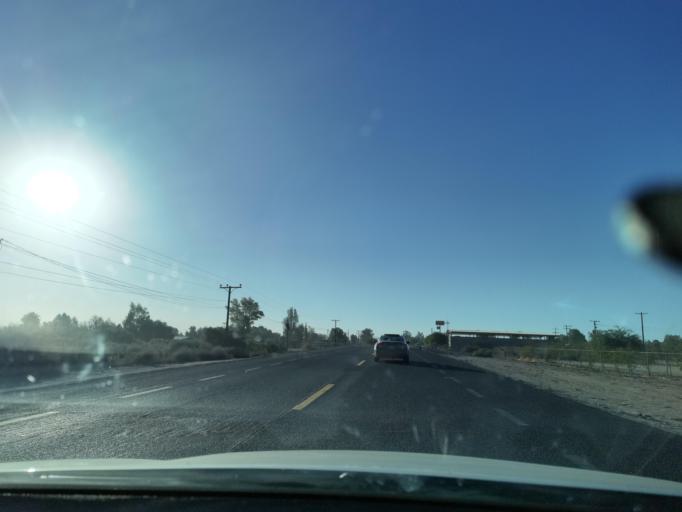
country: MX
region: Baja California
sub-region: Mexicali
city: Islas Agrarias Grupo A
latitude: 32.6459
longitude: -115.3220
